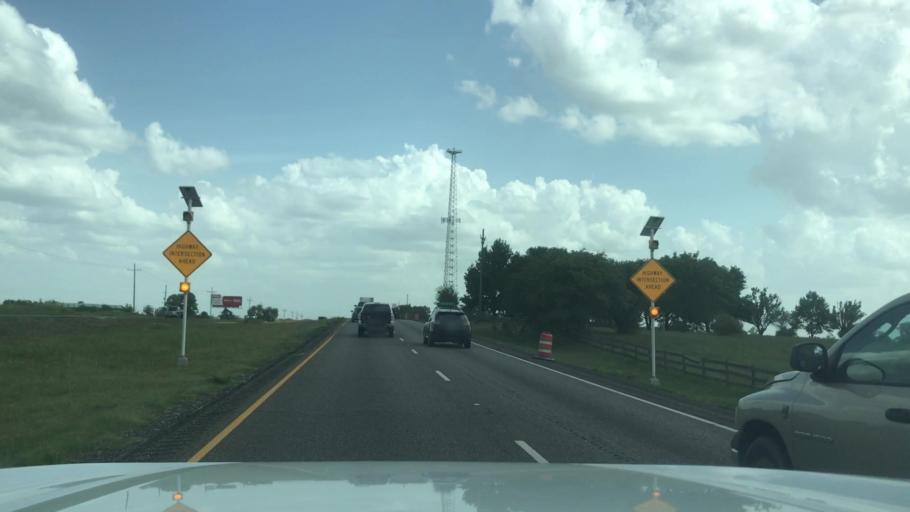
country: US
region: Texas
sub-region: Grimes County
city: Navasota
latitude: 30.2794
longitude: -96.0443
